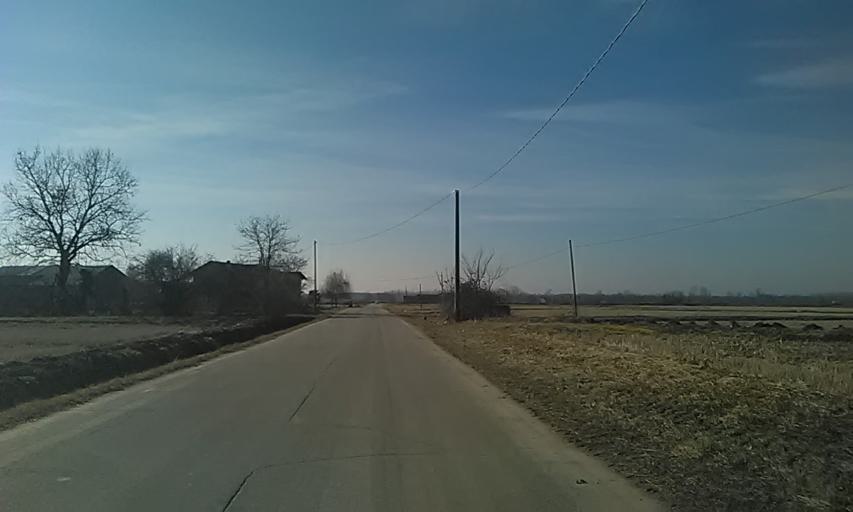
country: IT
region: Piedmont
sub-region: Provincia di Vercelli
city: Balocco
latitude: 45.4637
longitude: 8.2833
